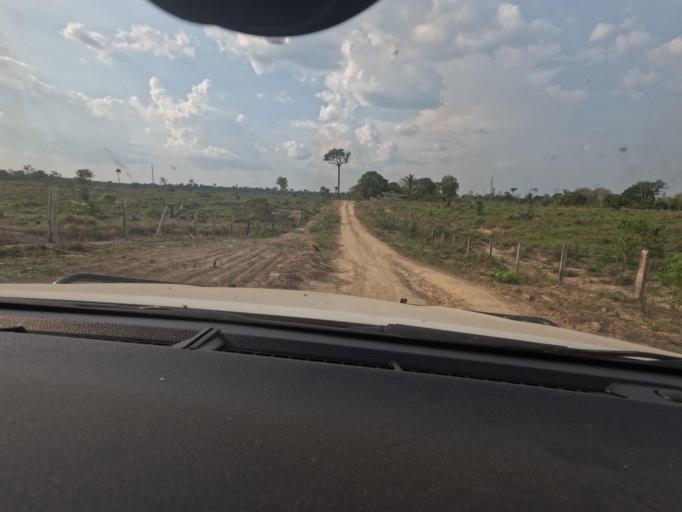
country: BR
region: Rondonia
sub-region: Porto Velho
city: Porto Velho
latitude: -8.6391
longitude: -63.1556
